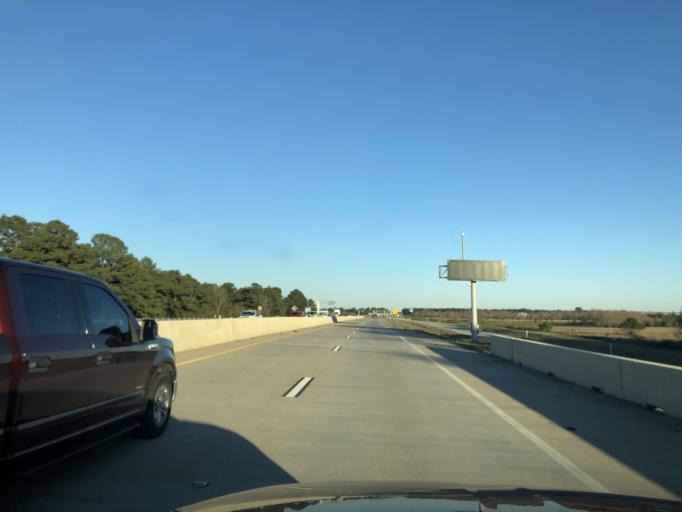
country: US
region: Texas
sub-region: Harris County
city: Tomball
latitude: 30.0510
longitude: -95.6542
